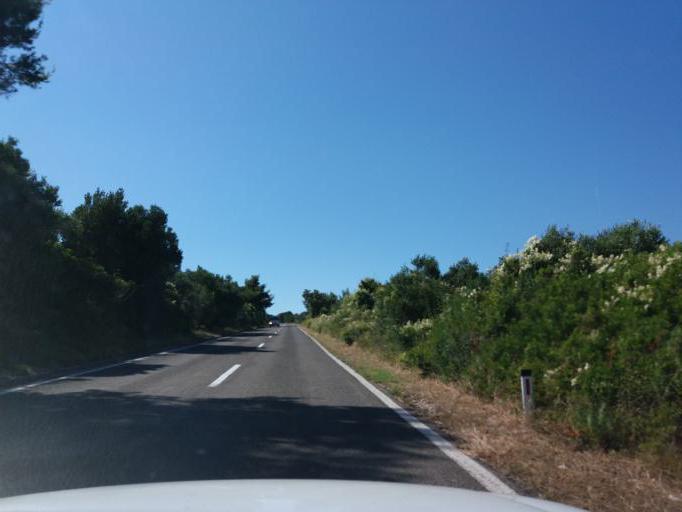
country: HR
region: Zadarska
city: Ugljan
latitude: 44.0745
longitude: 14.9943
